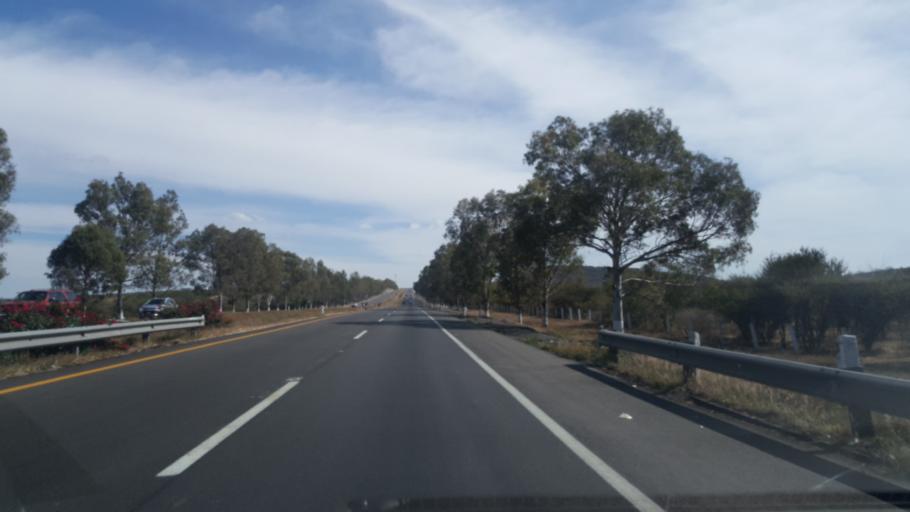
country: MX
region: Jalisco
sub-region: Lagos de Moreno
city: Cristeros [Fraccionamiento]
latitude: 21.2710
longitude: -101.9745
